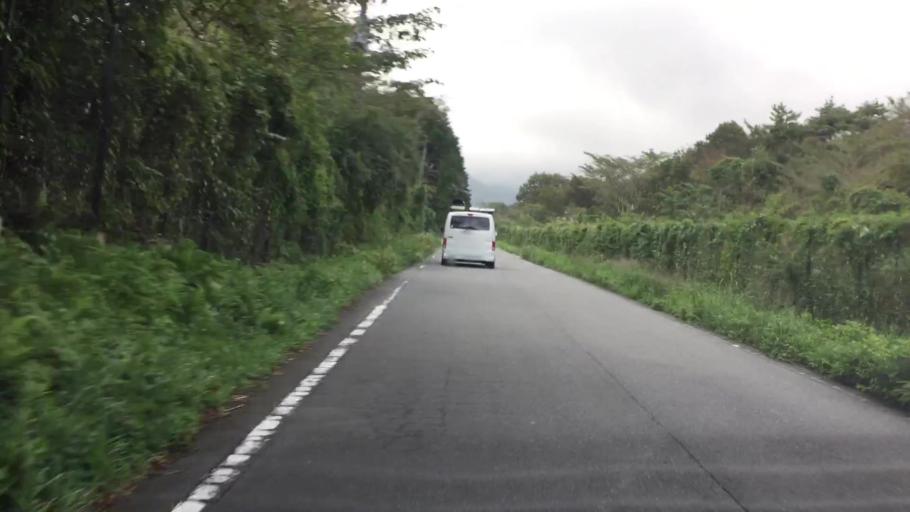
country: JP
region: Shizuoka
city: Fujinomiya
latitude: 35.3676
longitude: 138.5850
